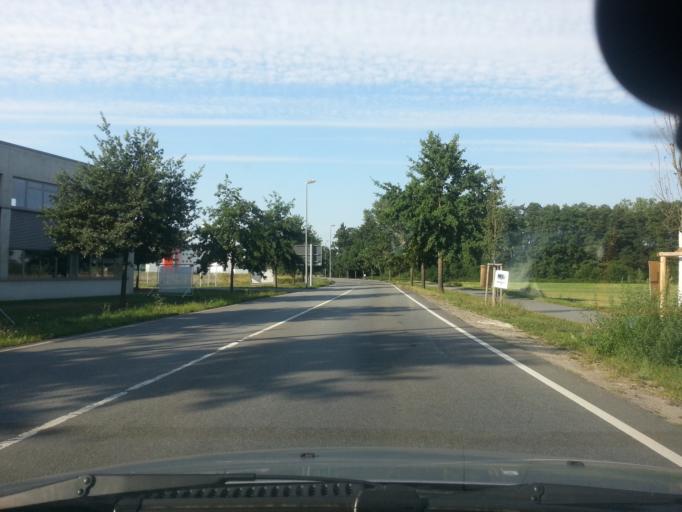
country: DE
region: Hesse
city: Lorsch
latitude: 49.6747
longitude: 8.5864
